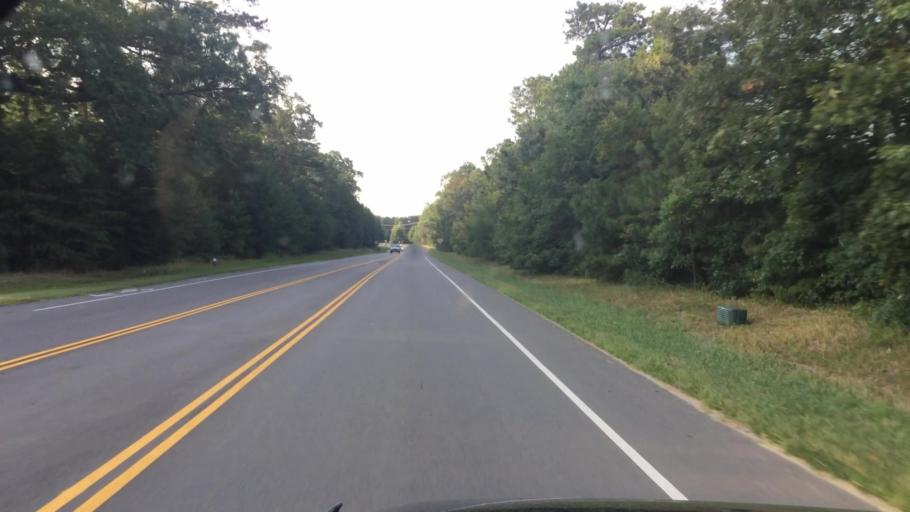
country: US
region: Virginia
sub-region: City of Williamsburg
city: Williamsburg
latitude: 37.2919
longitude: -76.7224
